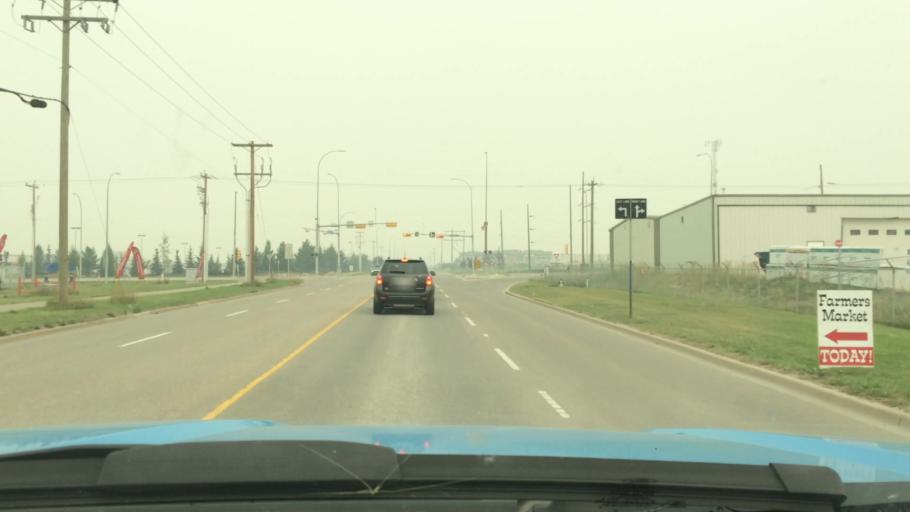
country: CA
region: Alberta
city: Airdrie
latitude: 51.2988
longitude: -113.9900
